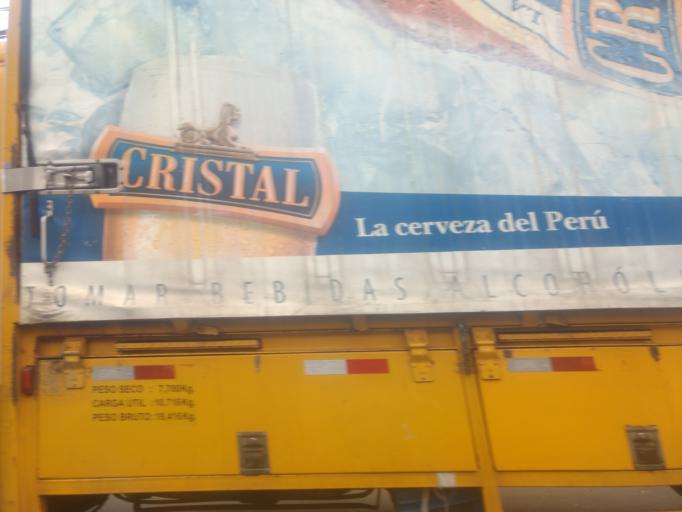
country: PE
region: Callao
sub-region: Callao
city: Callao
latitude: -12.0623
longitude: -77.0824
